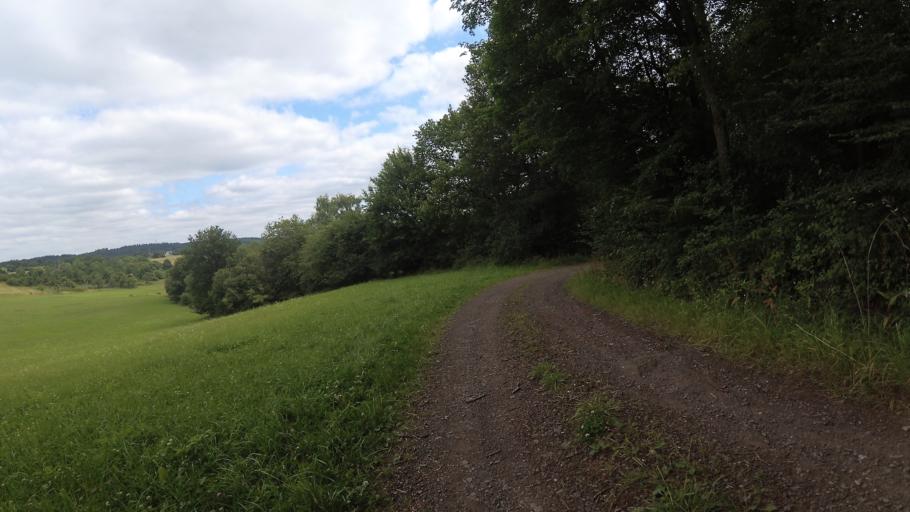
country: DE
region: Saarland
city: Mainzweiler
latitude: 49.4225
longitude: 7.1424
